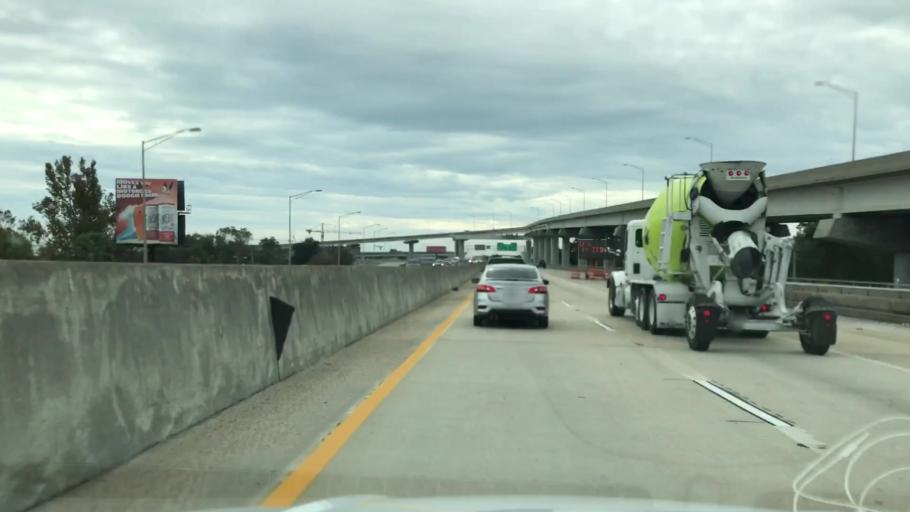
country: US
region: South Carolina
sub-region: Charleston County
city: Charleston
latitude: 32.8082
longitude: -79.9493
